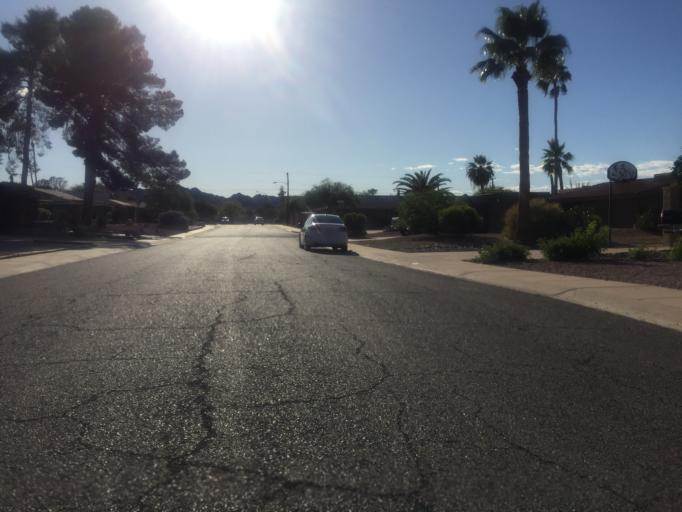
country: US
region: Arizona
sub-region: Maricopa County
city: Paradise Valley
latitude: 33.5794
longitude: -112.0076
